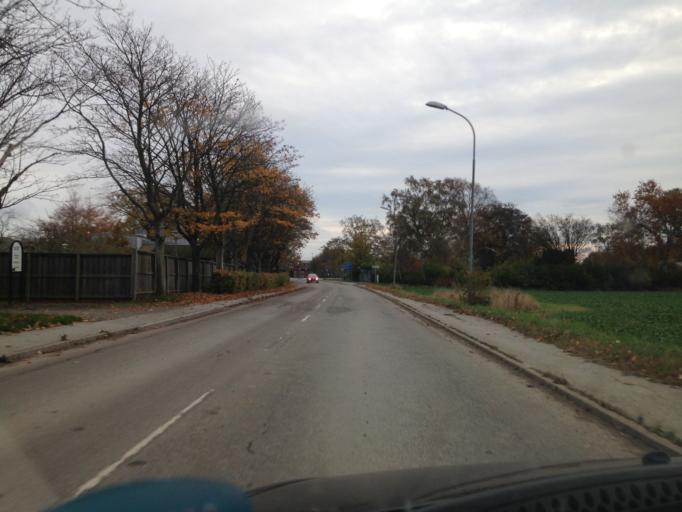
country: SE
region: Skane
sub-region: Ystads Kommun
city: Kopingebro
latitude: 55.4301
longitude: 14.1131
